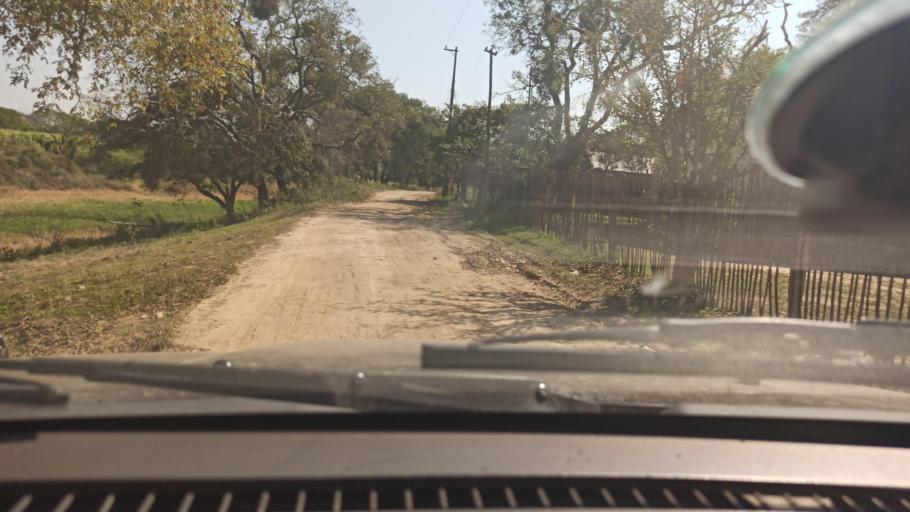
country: PY
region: Asuncion
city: Asuncion
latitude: -25.3316
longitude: -57.6839
